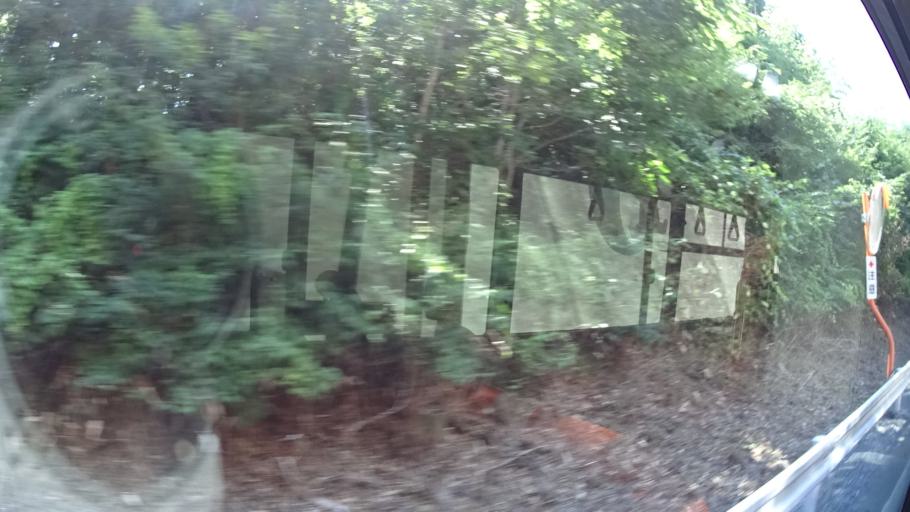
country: JP
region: Iwate
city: Ofunato
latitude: 39.0281
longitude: 141.7124
